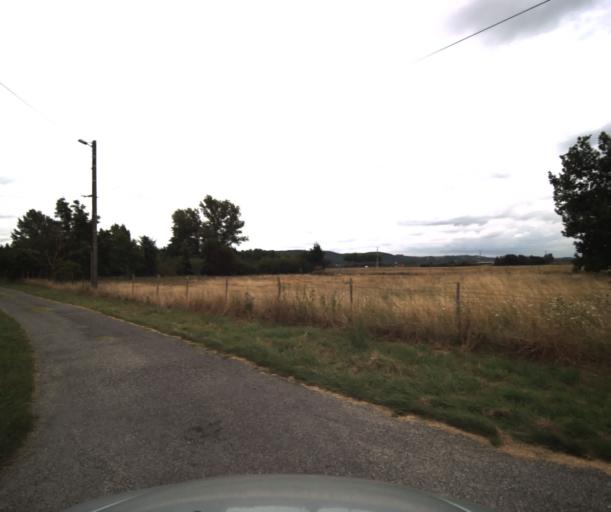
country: FR
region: Midi-Pyrenees
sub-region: Departement de la Haute-Garonne
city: Le Fauga
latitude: 43.4390
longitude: 1.3072
